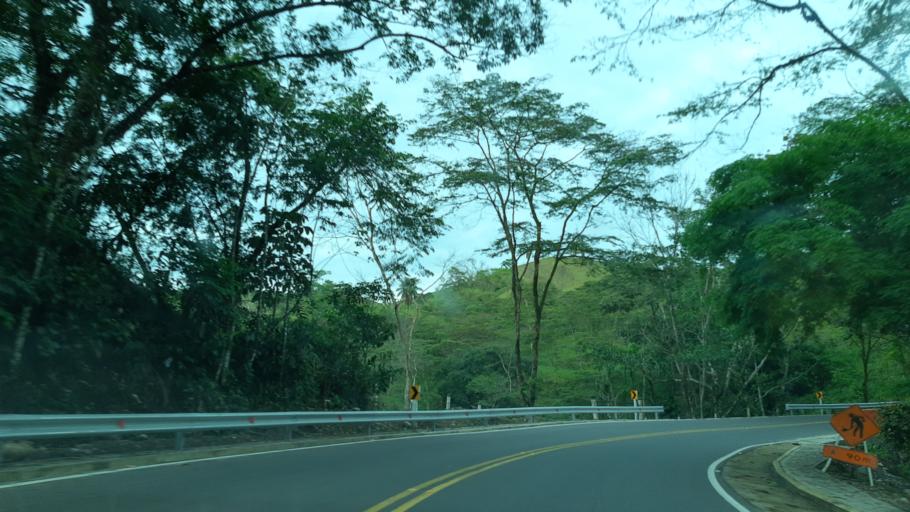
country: CO
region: Casanare
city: Sabanalarga
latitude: 4.7592
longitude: -73.0245
